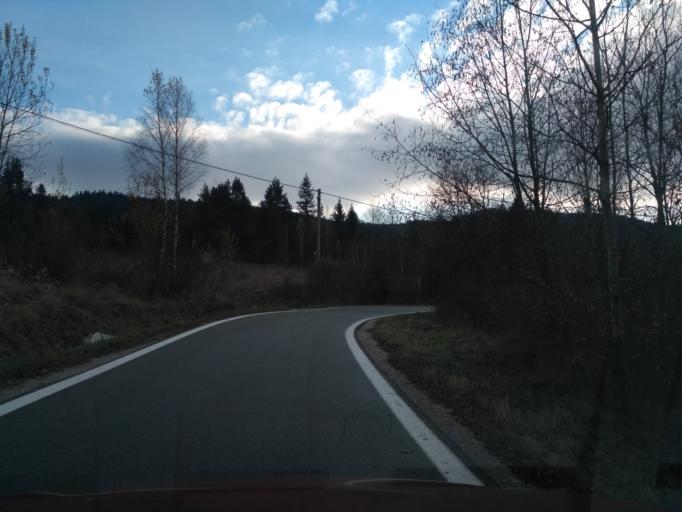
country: SK
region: Kosicky
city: Spisska Nova Ves
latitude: 48.8239
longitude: 20.6011
